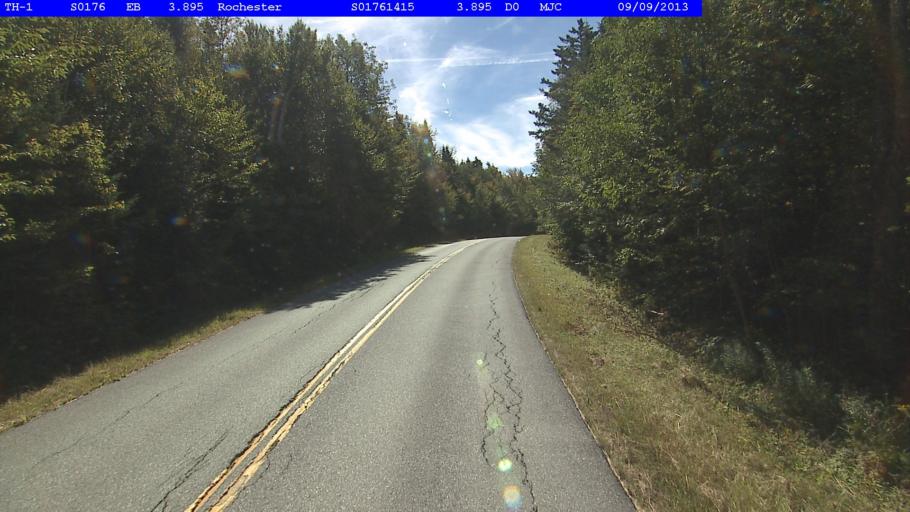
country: US
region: Vermont
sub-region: Orange County
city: Randolph
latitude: 43.8520
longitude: -72.7517
